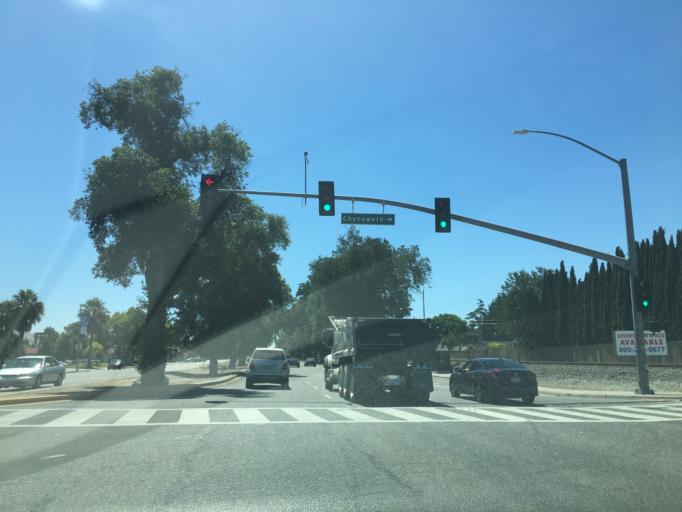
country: US
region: California
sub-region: Santa Clara County
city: Seven Trees
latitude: 37.2603
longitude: -121.8103
